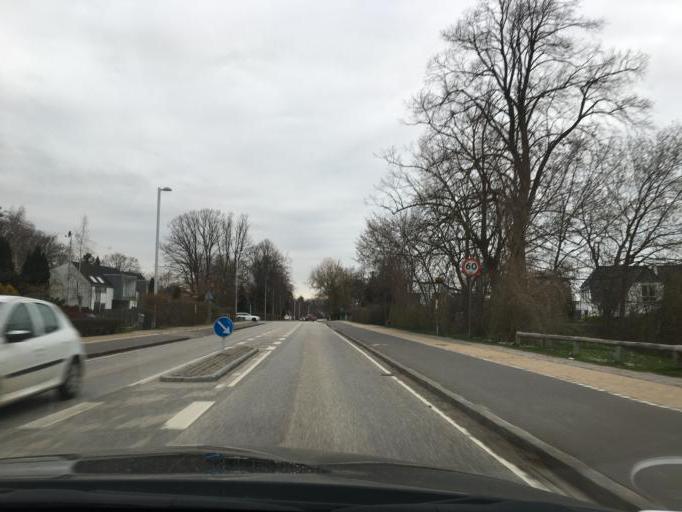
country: DK
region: Capital Region
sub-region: Fredensborg Kommune
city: Kokkedal
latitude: 55.9133
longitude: 12.5201
